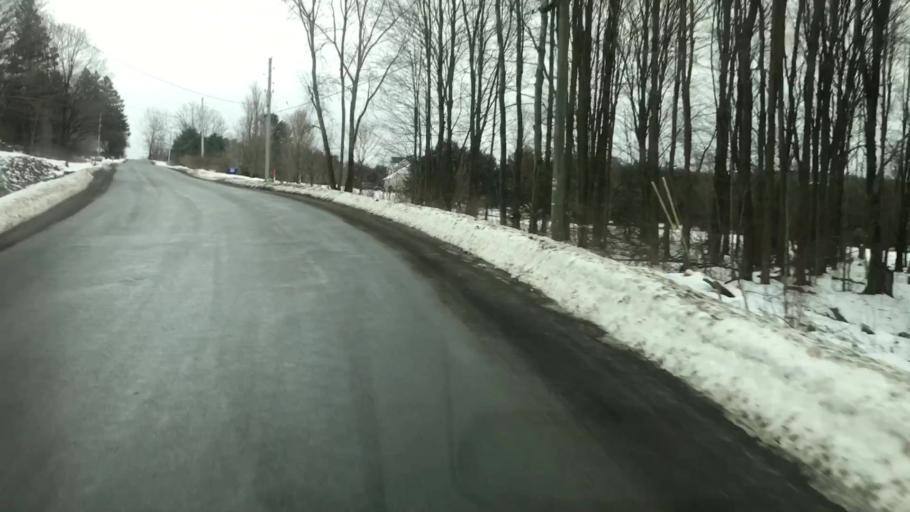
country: US
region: New York
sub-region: Cortland County
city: Cortland West
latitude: 42.6517
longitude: -76.2711
